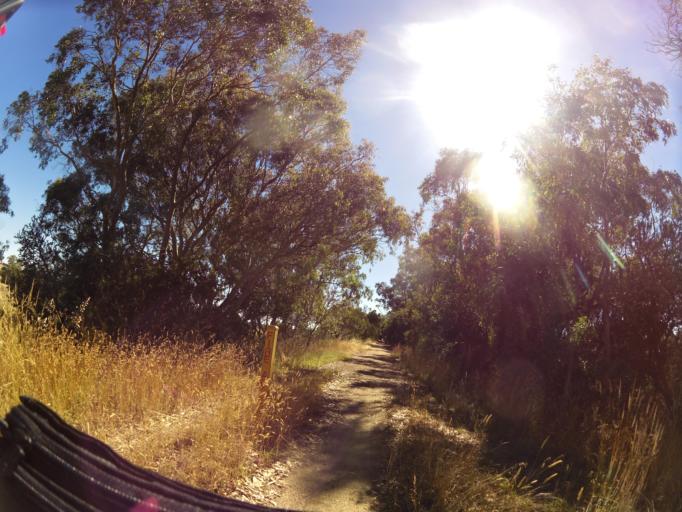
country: AU
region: Victoria
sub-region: Ballarat North
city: Delacombe
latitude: -37.6695
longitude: 143.4574
